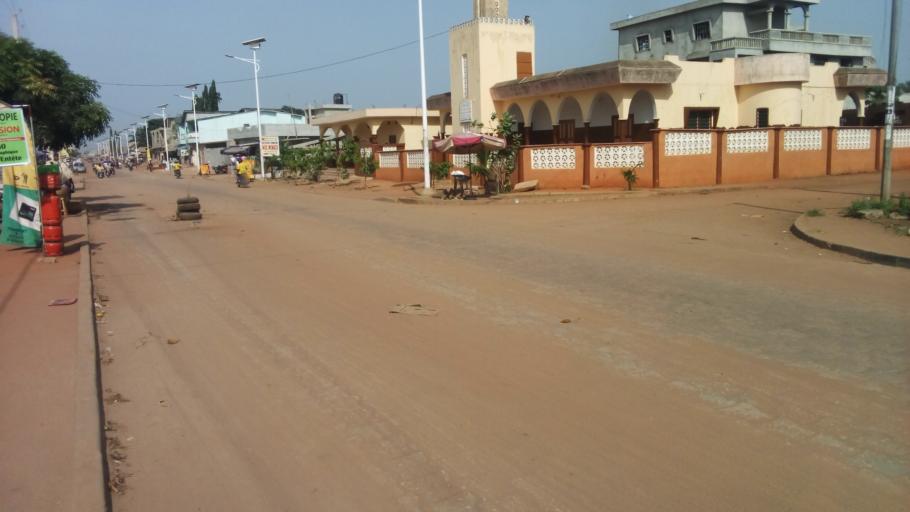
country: BJ
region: Atlantique
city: Abomey-Calavi
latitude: 6.4265
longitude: 2.3239
